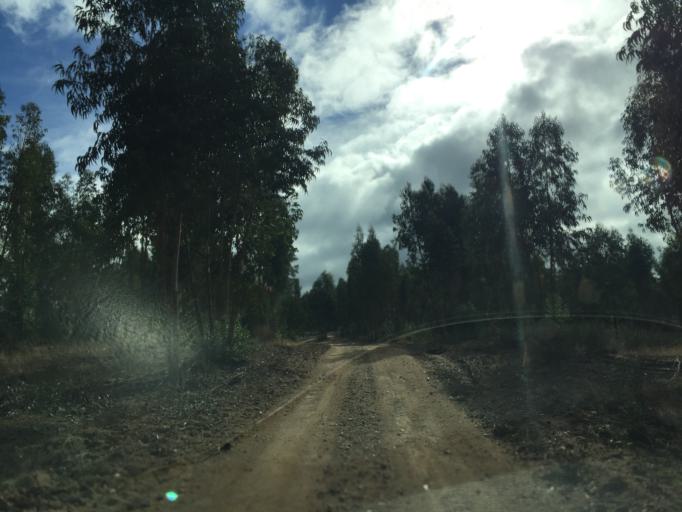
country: PT
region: Portalegre
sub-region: Alter do Chao
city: Alter do Chao
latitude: 39.2474
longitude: -7.7091
